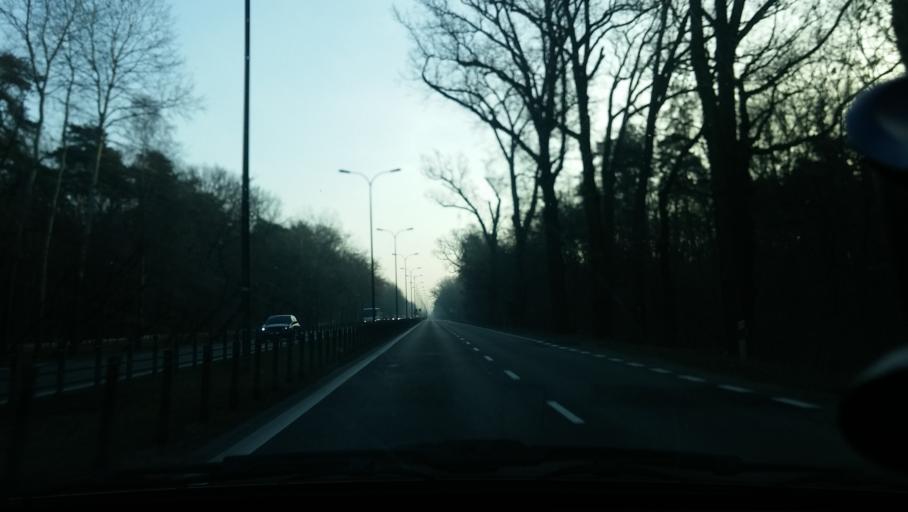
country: PL
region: Masovian Voivodeship
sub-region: Warszawa
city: Wawer
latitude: 52.2256
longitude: 21.1713
